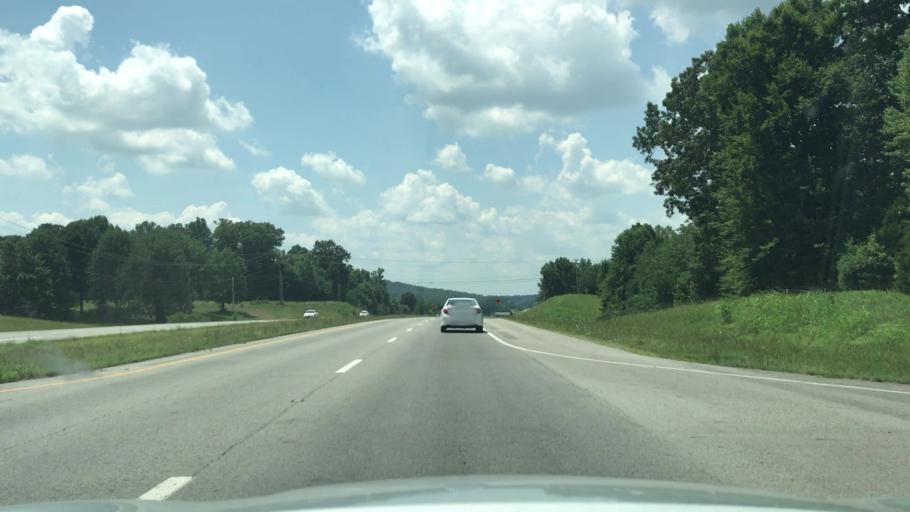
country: US
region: Tennessee
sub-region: Overton County
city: Livingston
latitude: 36.3414
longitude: -85.3486
